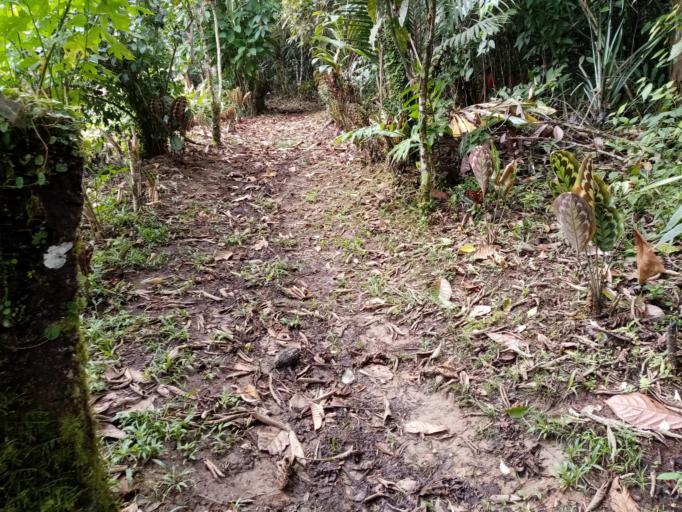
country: EC
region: Napo
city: Tena
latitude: -0.9716
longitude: -77.8004
